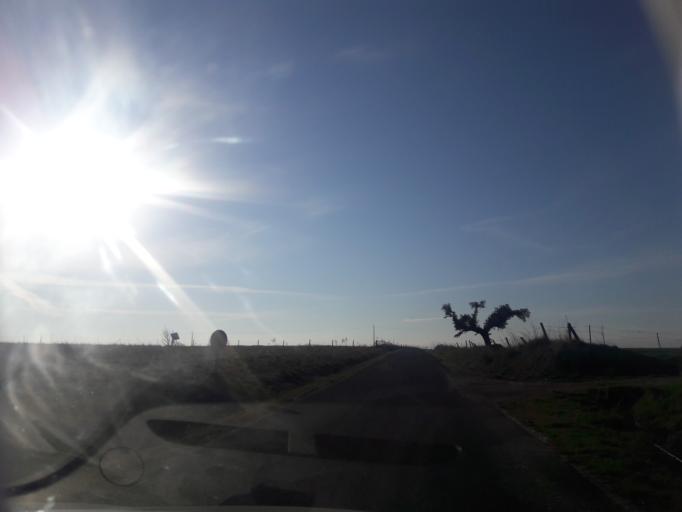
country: ES
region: Castille and Leon
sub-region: Provincia de Salamanca
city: Salvatierra de Tormes
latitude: 40.6132
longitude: -5.6054
